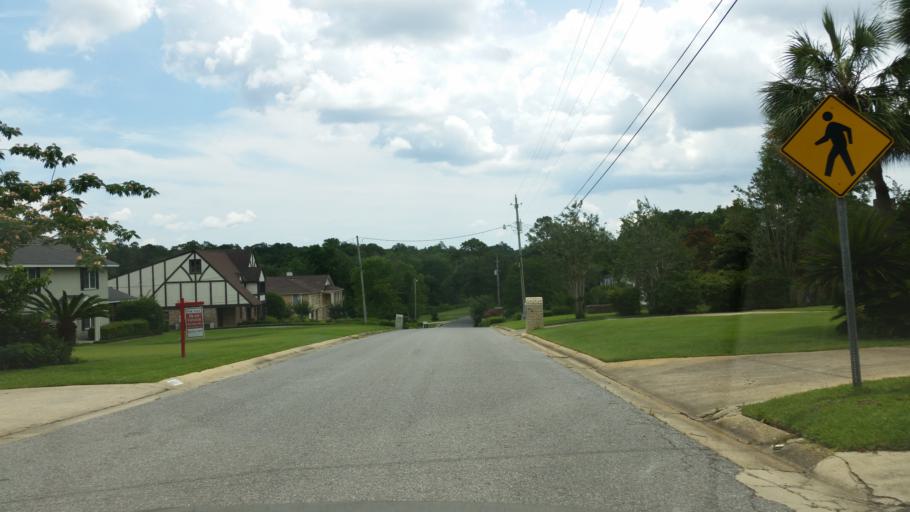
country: US
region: Florida
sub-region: Escambia County
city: Ferry Pass
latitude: 30.5430
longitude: -87.2327
